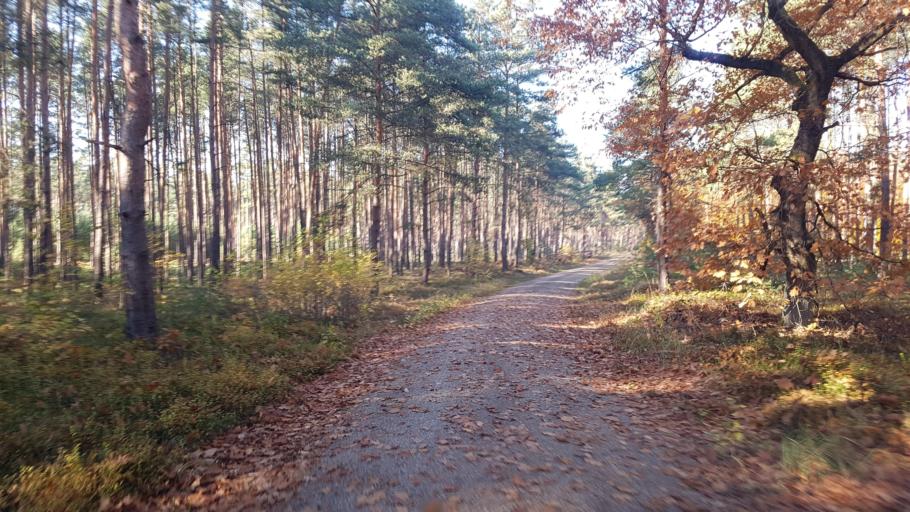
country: DE
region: Brandenburg
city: Ruckersdorf
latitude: 51.5681
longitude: 13.6149
